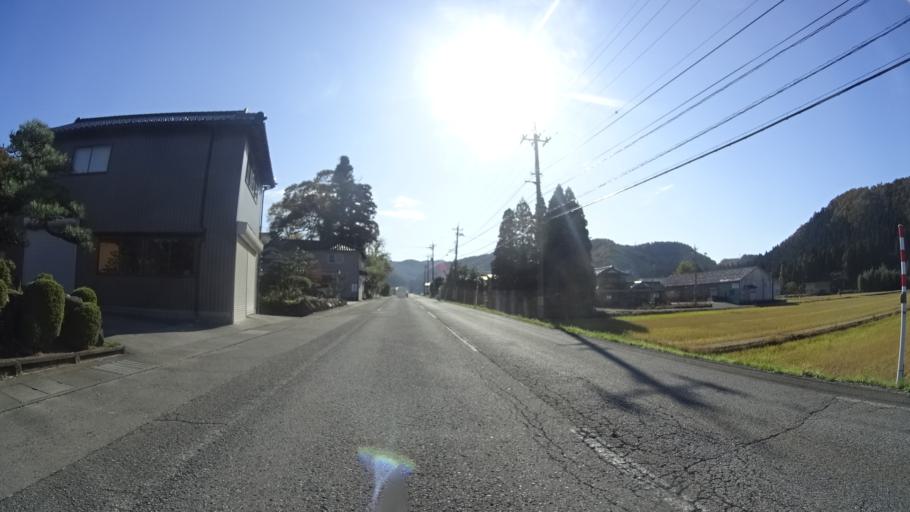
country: JP
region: Ishikawa
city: Komatsu
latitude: 36.3843
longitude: 136.5310
